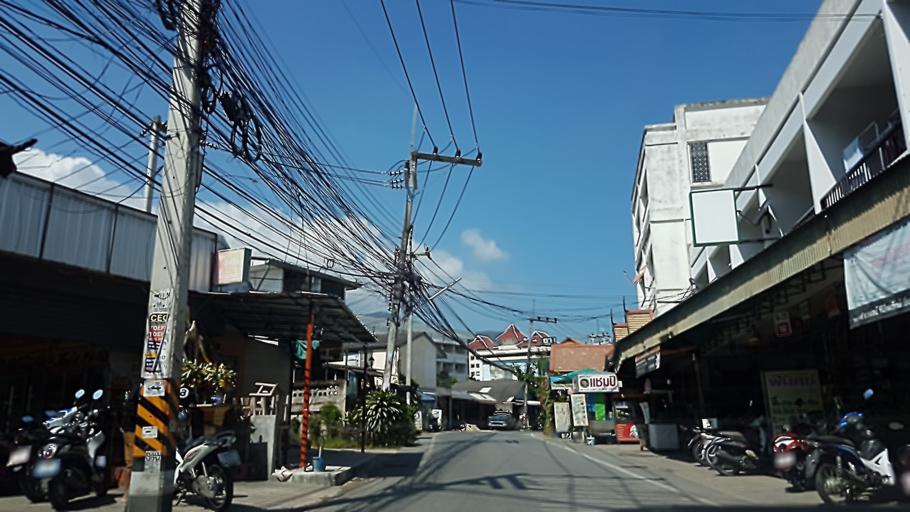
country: TH
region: Chiang Mai
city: Chiang Mai
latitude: 18.8110
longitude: 98.9583
